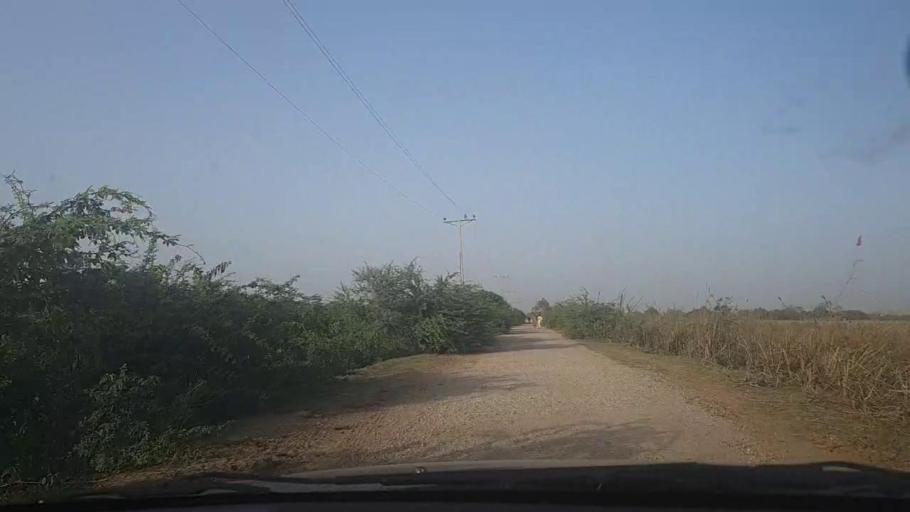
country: PK
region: Sindh
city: Keti Bandar
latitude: 24.2865
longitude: 67.6042
